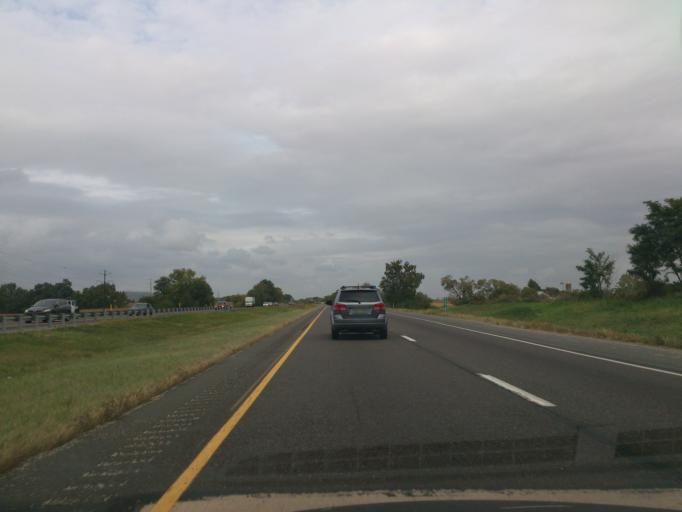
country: US
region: Pennsylvania
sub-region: Lancaster County
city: Ephrata
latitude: 40.1519
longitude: -76.1630
